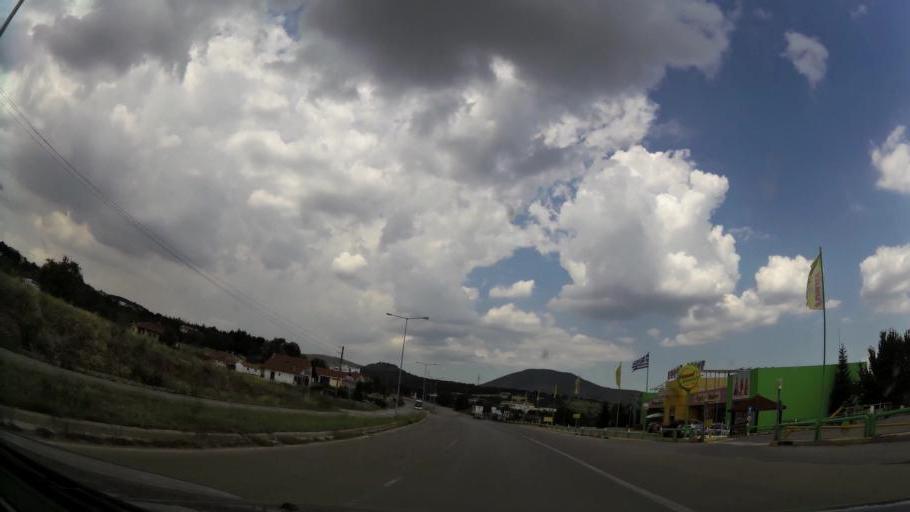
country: GR
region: West Macedonia
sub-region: Nomos Kozanis
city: Kozani
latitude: 40.3121
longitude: 21.8229
